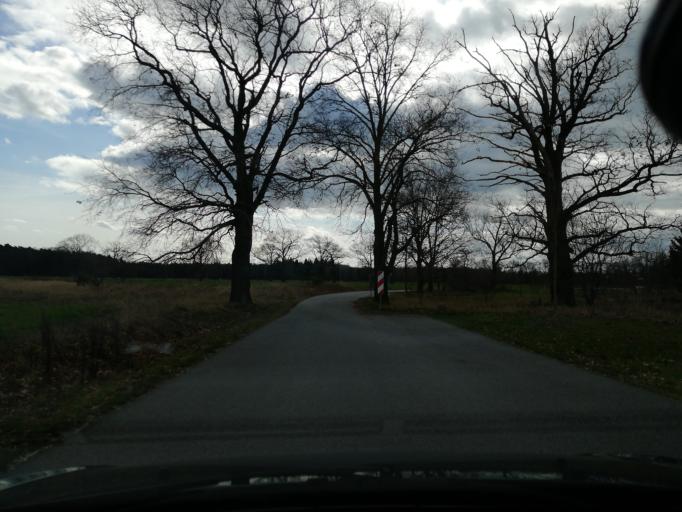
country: DE
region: Brandenburg
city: Altdobern
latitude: 51.6908
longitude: 14.1021
